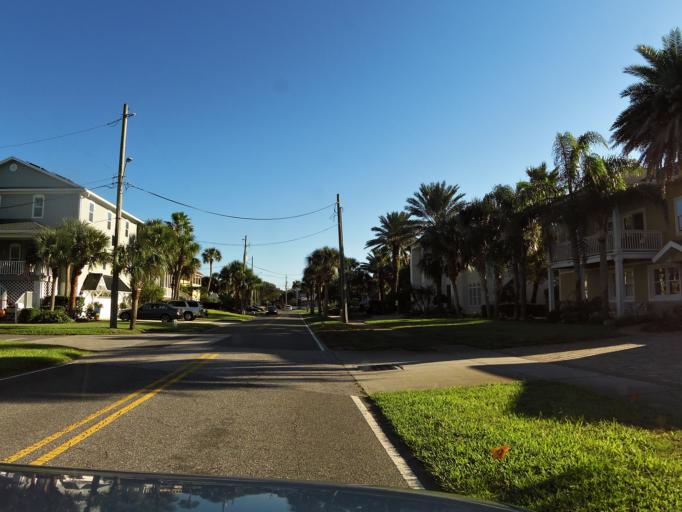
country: US
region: Florida
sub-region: Duval County
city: Atlantic Beach
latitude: 30.3381
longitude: -81.3989
